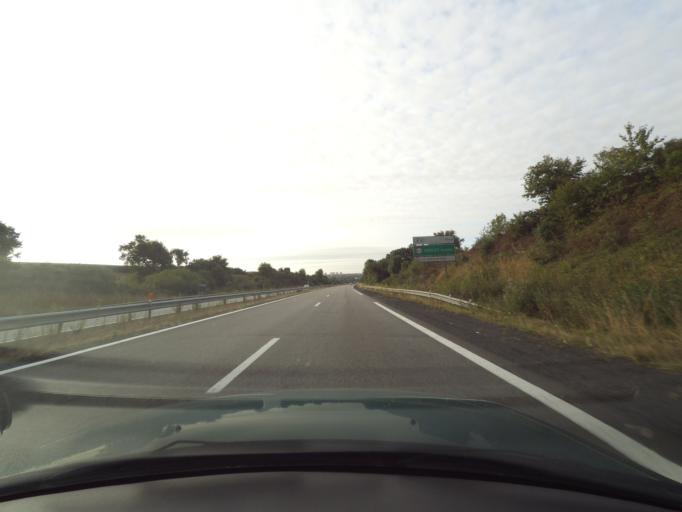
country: FR
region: Pays de la Loire
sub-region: Departement de Maine-et-Loire
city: La Seguiniere
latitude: 47.0673
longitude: -0.9319
